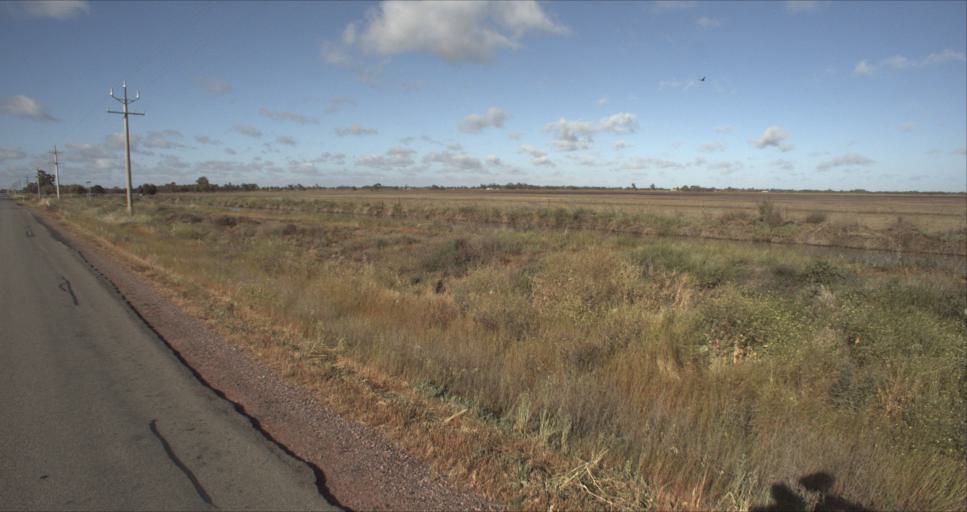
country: AU
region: New South Wales
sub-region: Leeton
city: Leeton
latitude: -34.5250
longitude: 146.3898
